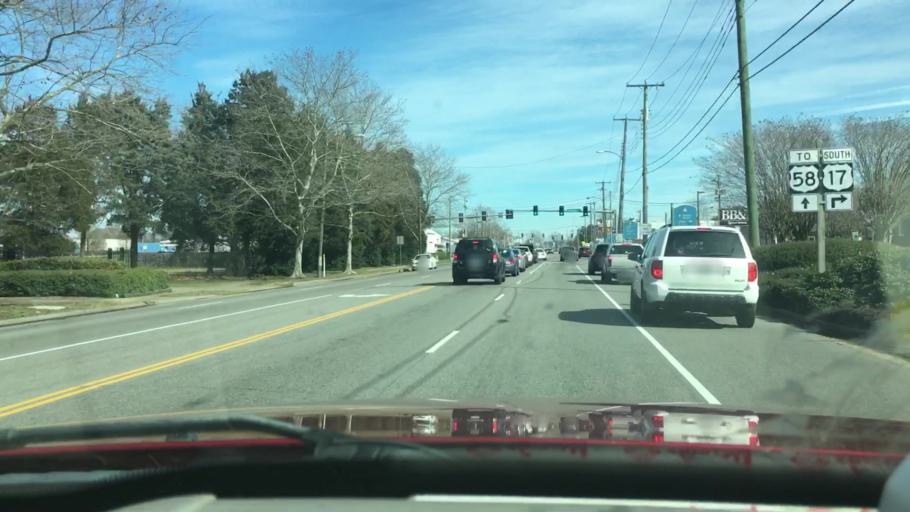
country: US
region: Virginia
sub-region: City of Portsmouth
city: Portsmouth Heights
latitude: 36.8343
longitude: -76.3431
